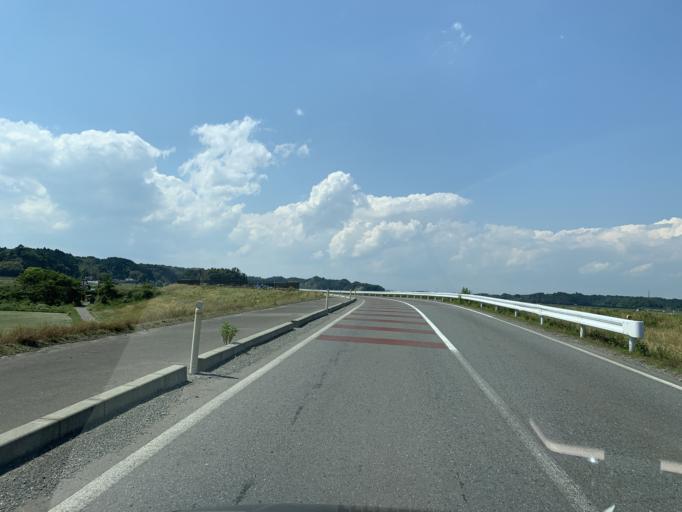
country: JP
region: Miyagi
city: Yamoto
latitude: 38.3883
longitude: 141.1617
